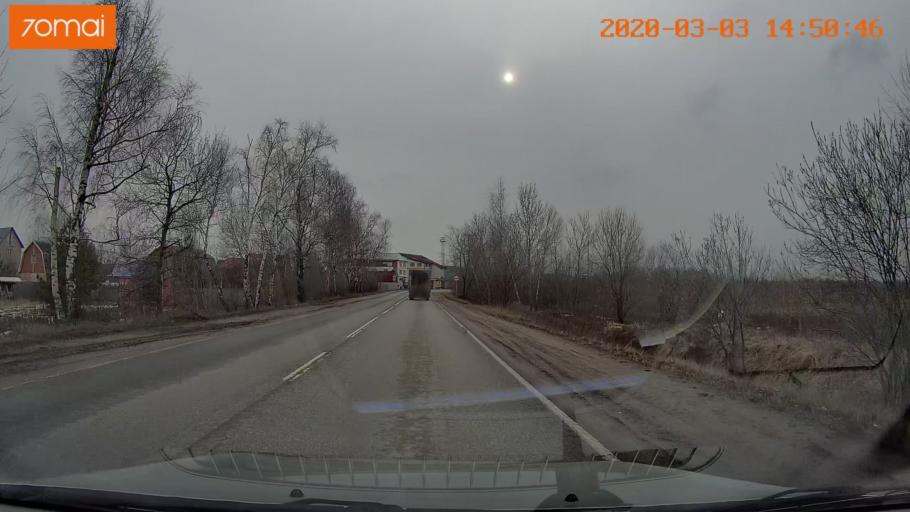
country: RU
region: Moskovskaya
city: Malakhovka
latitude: 55.6683
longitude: 38.0368
